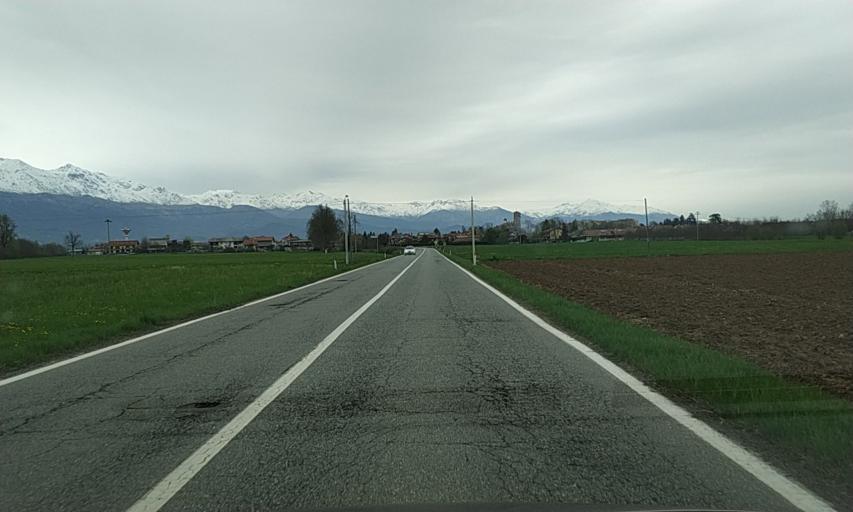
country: IT
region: Piedmont
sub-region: Provincia di Torino
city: Favria
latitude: 45.3228
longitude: 7.6845
